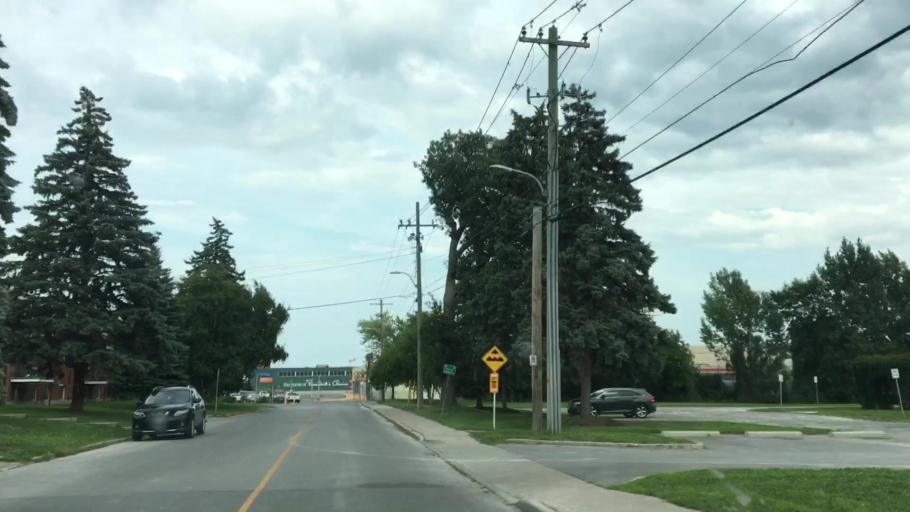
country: CA
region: Ontario
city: Quinte West
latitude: 44.1034
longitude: -77.5579
